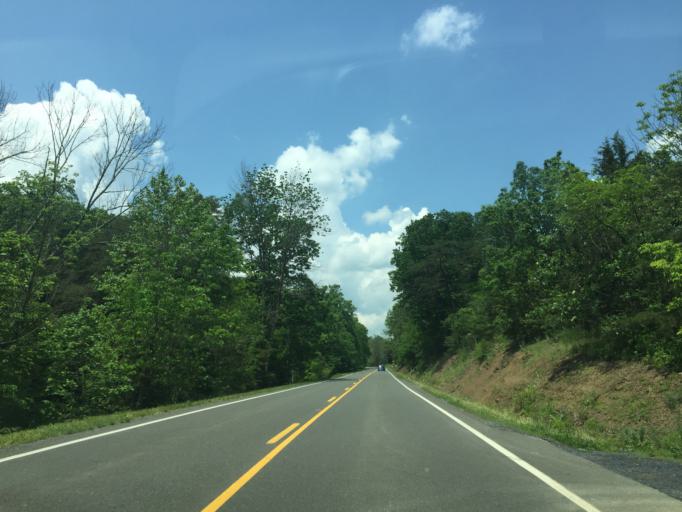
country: US
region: Virginia
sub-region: Shenandoah County
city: Strasburg
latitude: 39.0785
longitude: -78.3805
